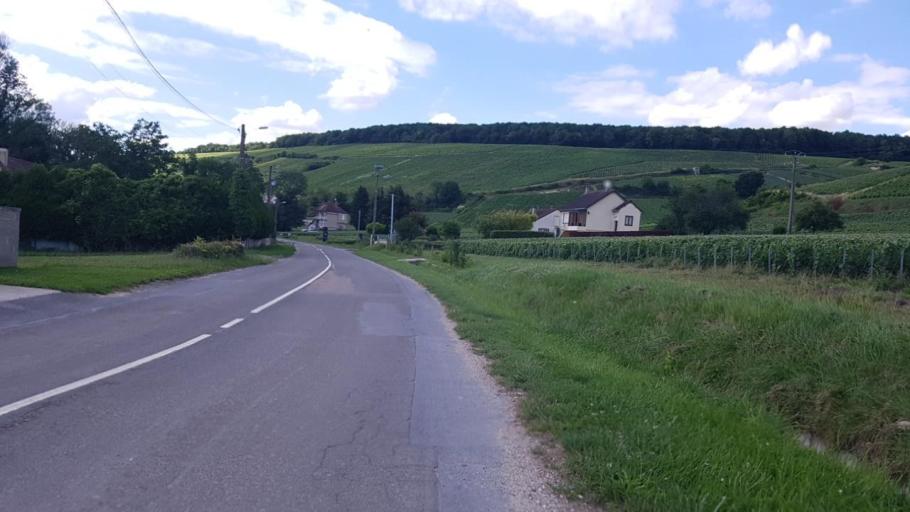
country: FR
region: Picardie
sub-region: Departement de l'Aisne
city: Crezancy
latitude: 49.0818
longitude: 3.5592
